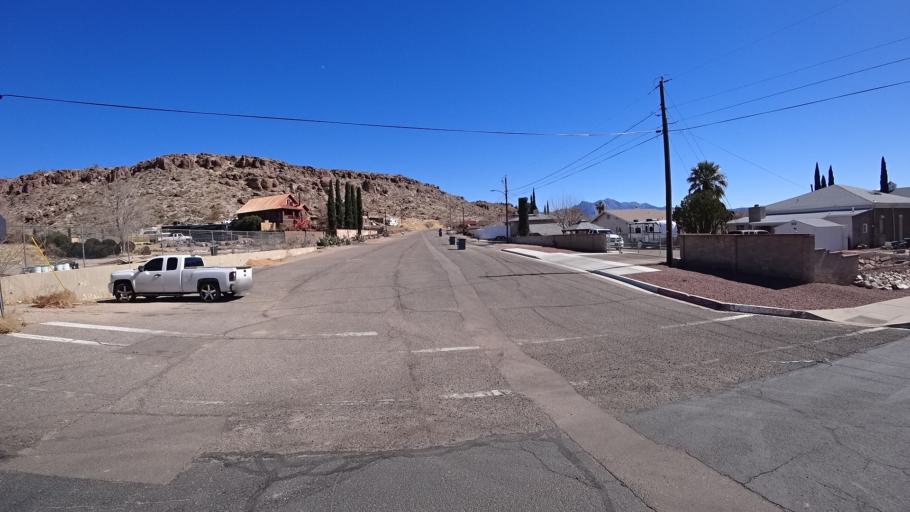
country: US
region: Arizona
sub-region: Mohave County
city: Kingman
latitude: 35.1921
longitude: -114.0509
